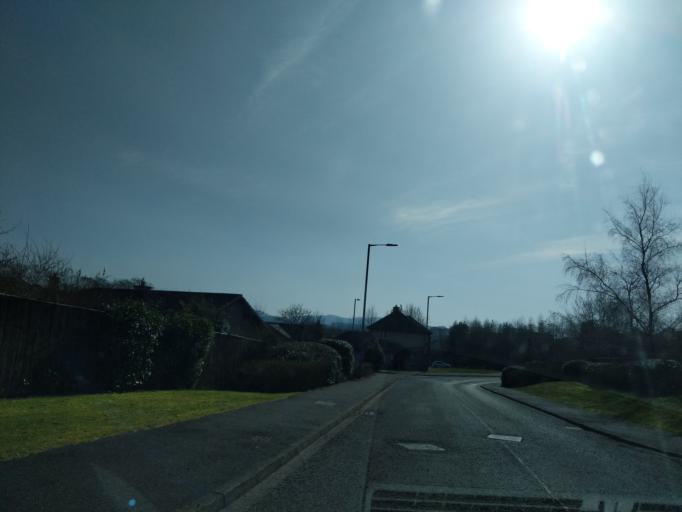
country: GB
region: Scotland
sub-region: The Scottish Borders
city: West Linton
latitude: 55.7564
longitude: -3.3481
